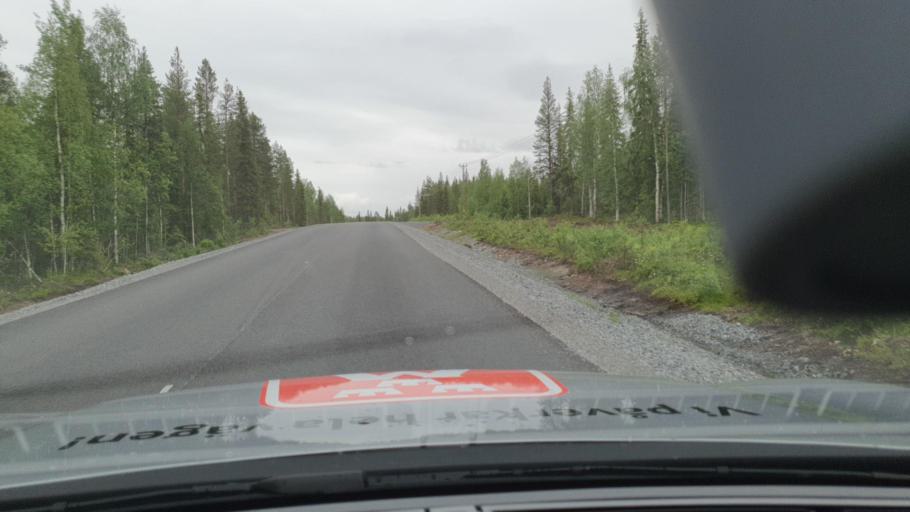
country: SE
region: Norrbotten
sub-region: Overkalix Kommun
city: OEverkalix
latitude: 66.6631
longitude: 23.2186
